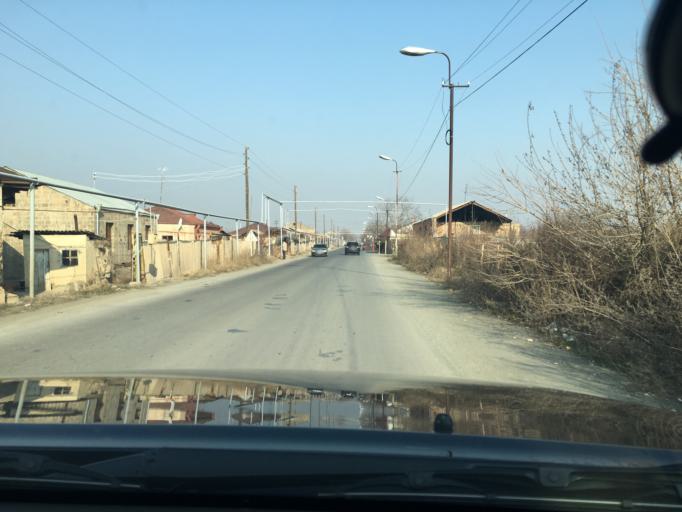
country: AM
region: Armavir
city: Sovetakan
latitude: 40.0898
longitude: 44.0452
